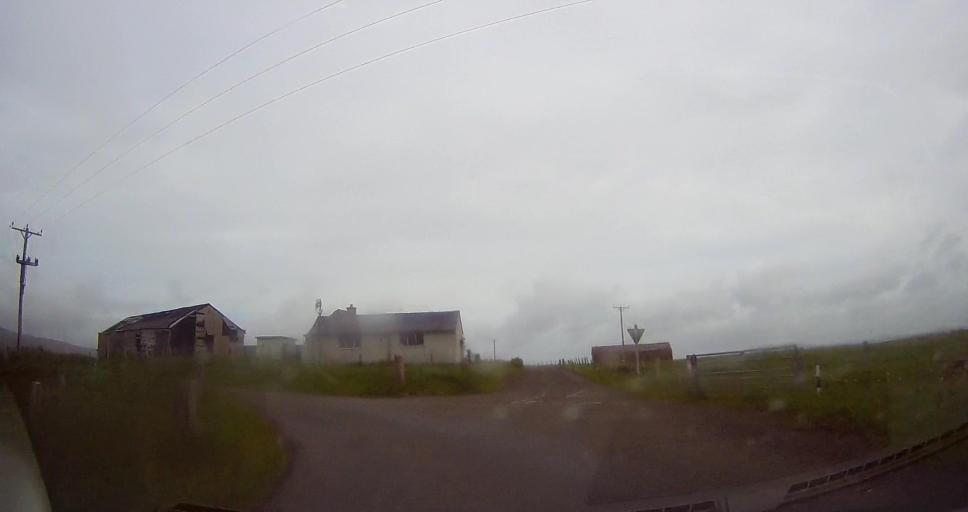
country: GB
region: Scotland
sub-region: Orkney Islands
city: Stromness
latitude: 58.8331
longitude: -3.2069
